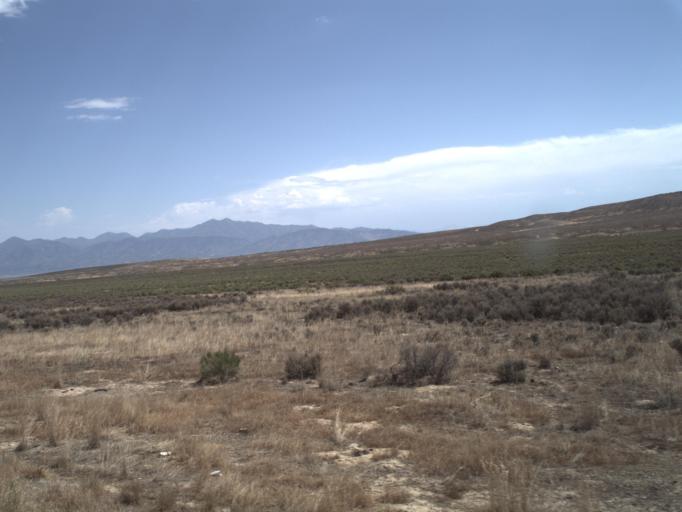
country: US
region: Utah
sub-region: Tooele County
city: Tooele
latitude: 40.1272
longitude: -112.4308
